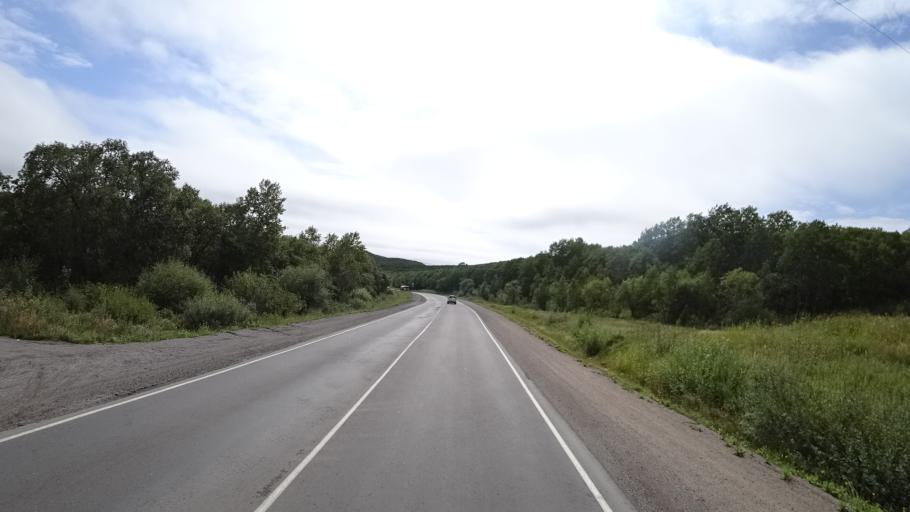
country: RU
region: Primorskiy
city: Lyalichi
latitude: 44.1216
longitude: 132.4207
